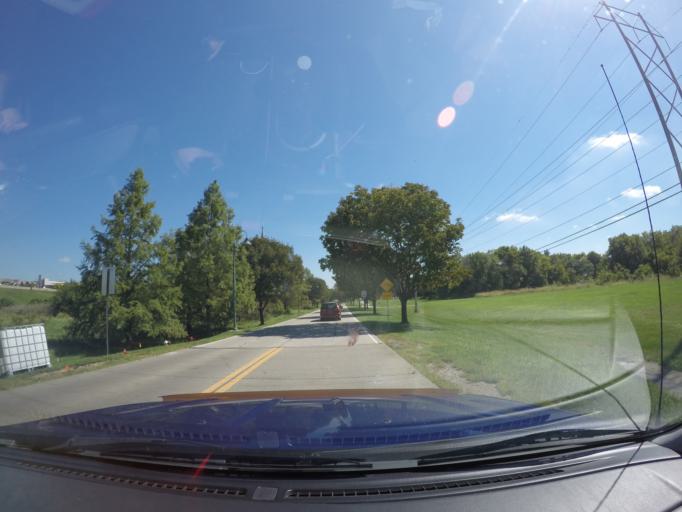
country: US
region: Kansas
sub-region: Johnson County
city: Leawood
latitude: 38.9318
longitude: -94.6298
